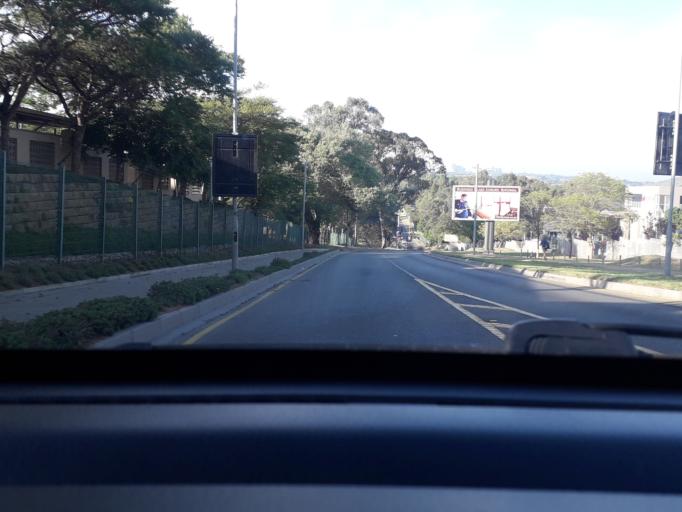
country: ZA
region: Gauteng
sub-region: City of Johannesburg Metropolitan Municipality
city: Midrand
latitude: -26.0597
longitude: 28.0837
